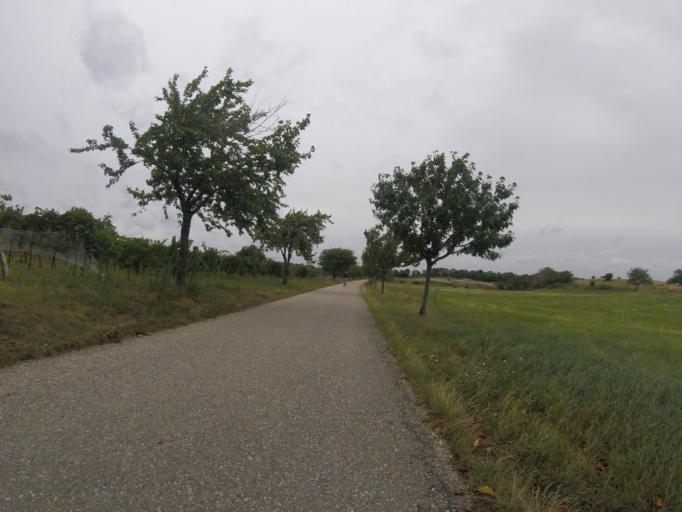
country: AT
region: Burgenland
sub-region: Eisenstadt-Umgebung
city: Breitenbrunn
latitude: 47.9424
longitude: 16.7118
